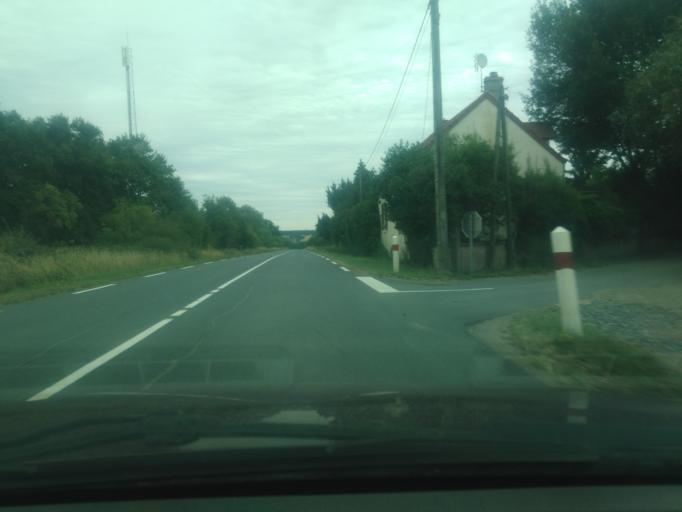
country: FR
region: Centre
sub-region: Departement de l'Indre
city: Cluis
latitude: 46.6026
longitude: 1.7207
